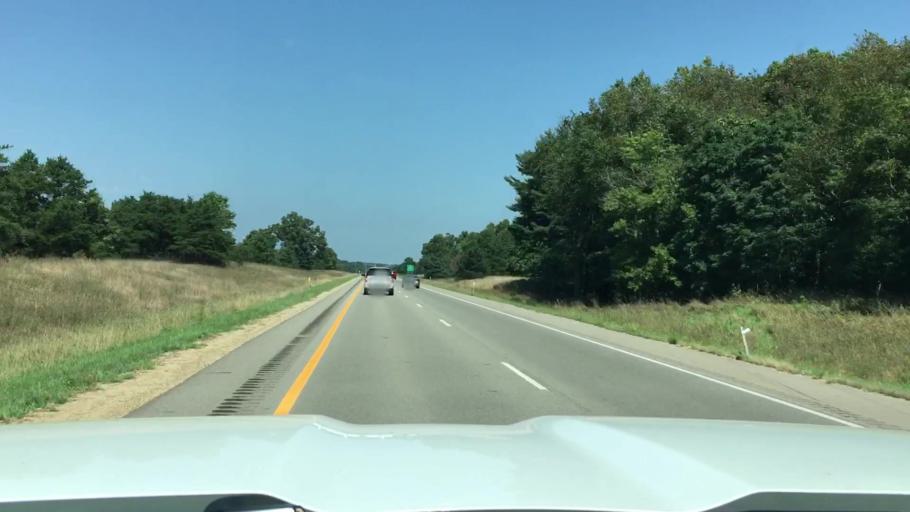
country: US
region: Michigan
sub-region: Kalamazoo County
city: Portage
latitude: 42.1833
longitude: -85.6457
